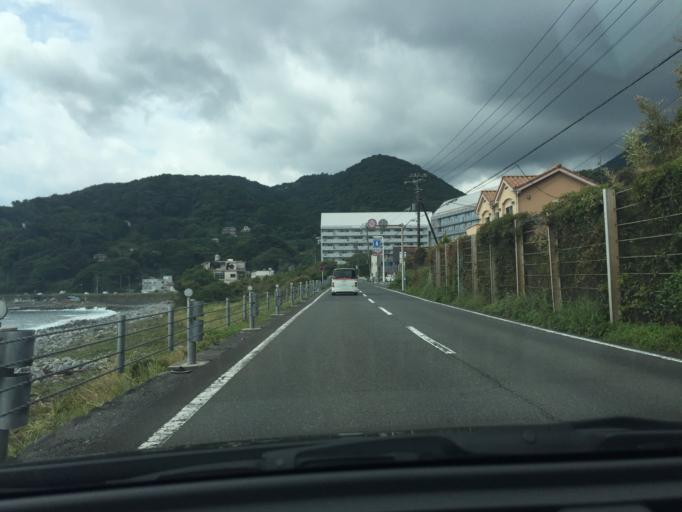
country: JP
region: Shizuoka
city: Ito
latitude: 34.8444
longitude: 139.0784
